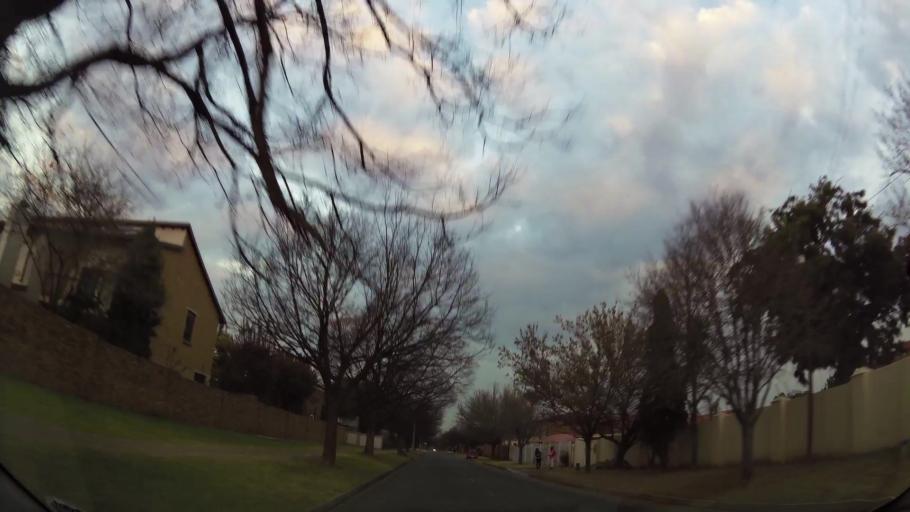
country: ZA
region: Gauteng
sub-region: Ekurhuleni Metropolitan Municipality
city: Benoni
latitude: -26.1740
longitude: 28.3068
